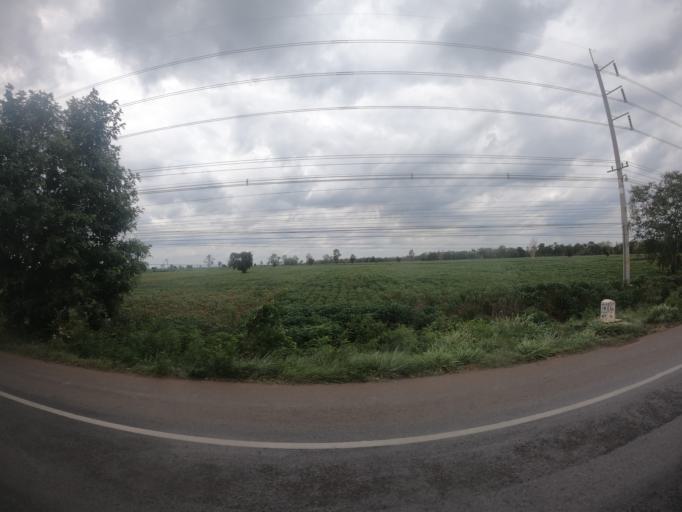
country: TH
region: Nakhon Ratchasima
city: Nong Bun Nak
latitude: 14.7402
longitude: 102.3712
